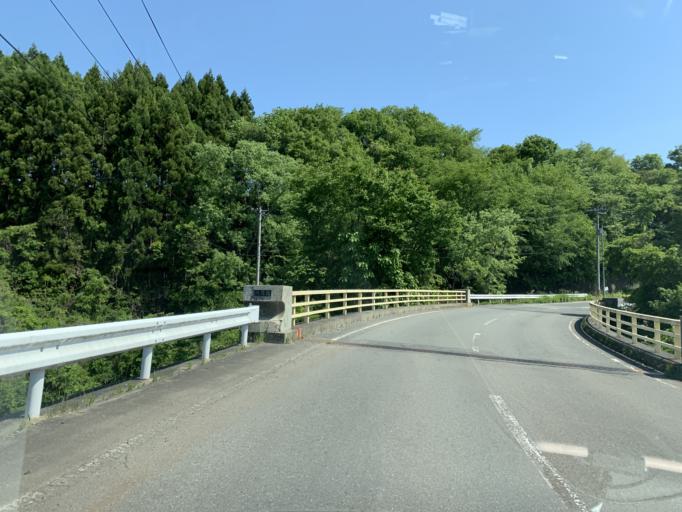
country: JP
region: Iwate
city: Mizusawa
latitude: 39.0640
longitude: 141.0605
